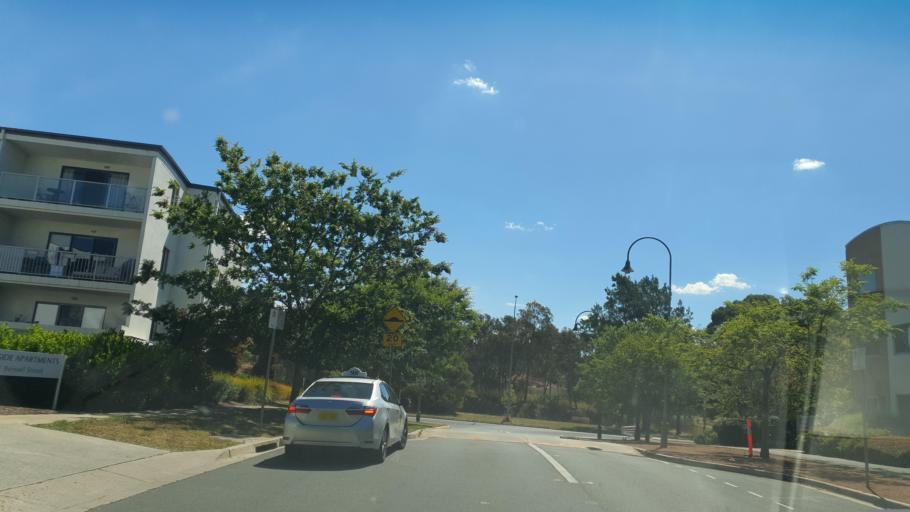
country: AU
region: Australian Capital Territory
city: Macquarie
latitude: -35.2340
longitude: 149.0632
